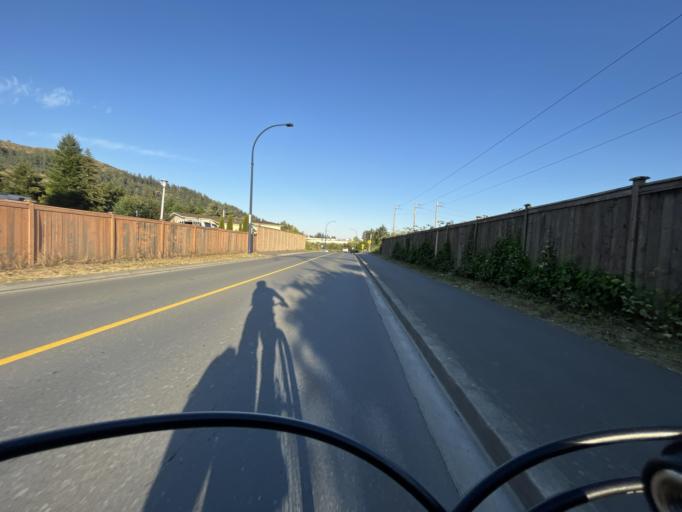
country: CA
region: British Columbia
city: Langford
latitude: 48.4589
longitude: -123.5461
